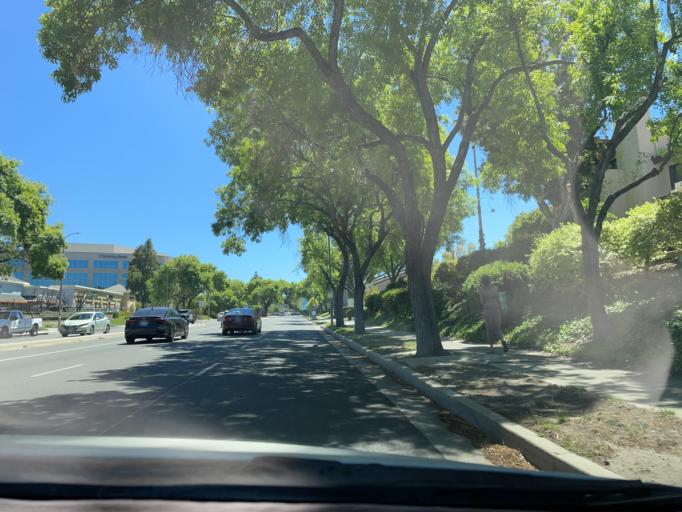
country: US
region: California
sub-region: Los Angeles County
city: Woodland Hills
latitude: 34.1759
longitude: -118.5975
